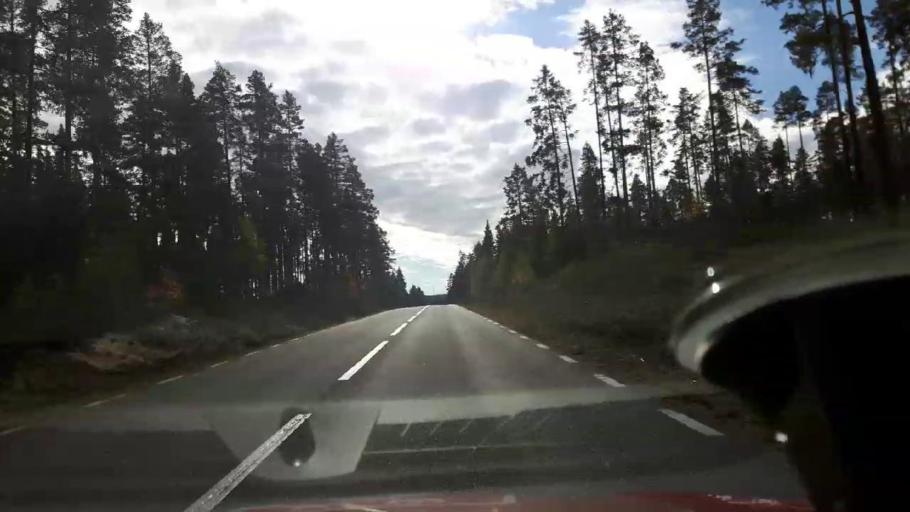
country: SE
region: Gaevleborg
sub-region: Ljusdals Kommun
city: Farila
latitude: 62.0225
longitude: 15.2287
